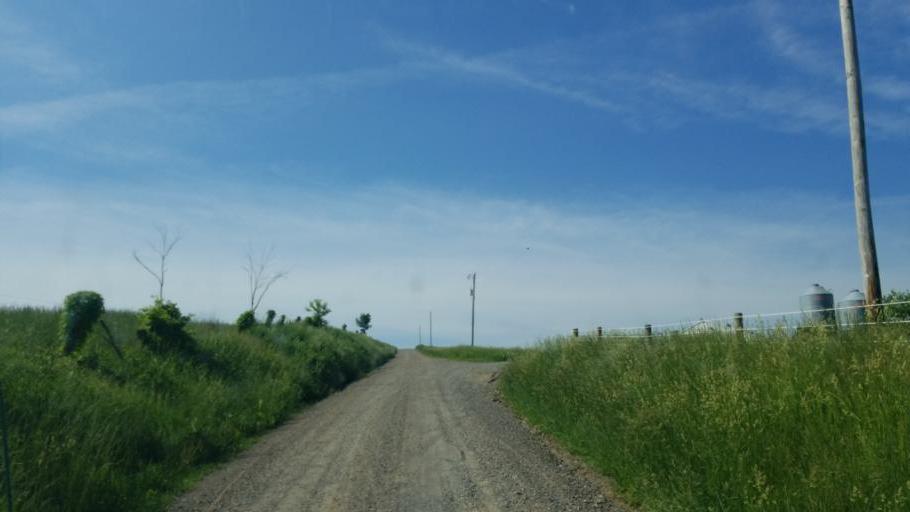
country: US
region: Ohio
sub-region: Tuscarawas County
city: Sugarcreek
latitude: 40.4717
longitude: -81.7562
